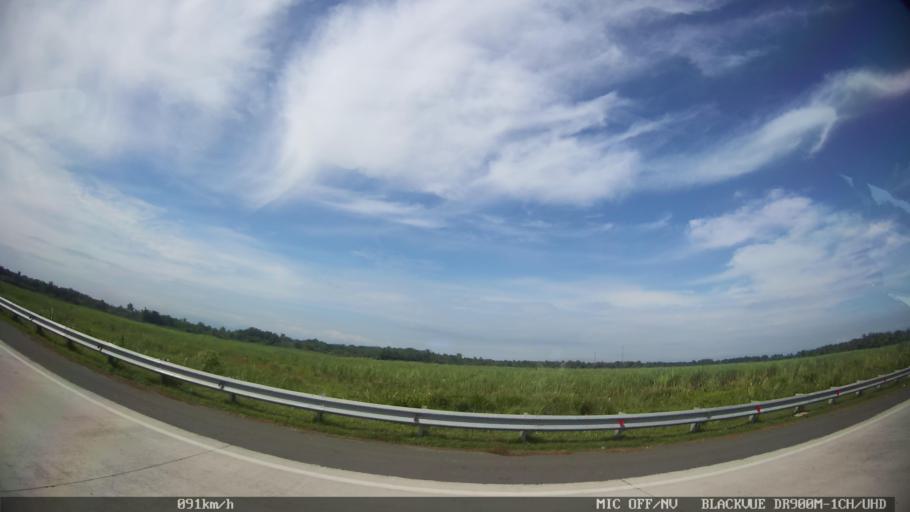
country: ID
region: North Sumatra
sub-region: Kabupaten Langkat
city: Stabat
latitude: 3.7083
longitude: 98.5351
